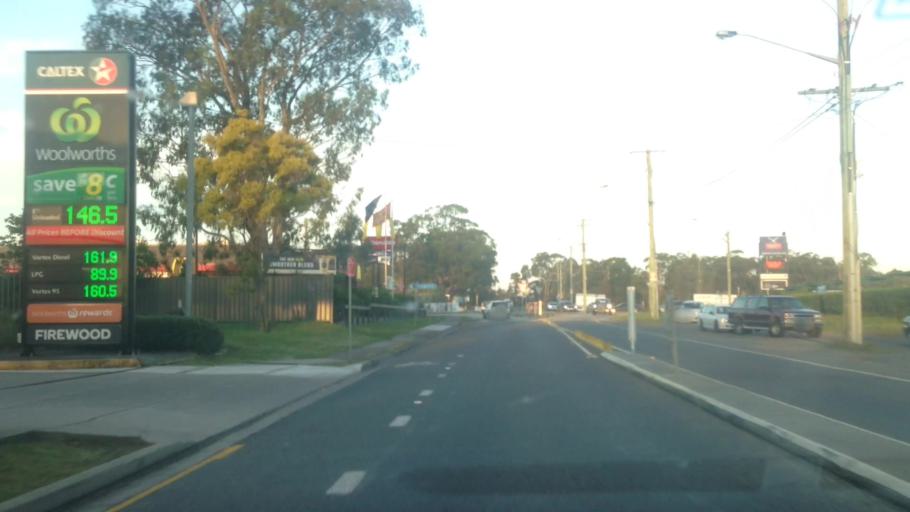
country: AU
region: New South Wales
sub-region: Lake Macquarie Shire
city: Dora Creek
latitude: -33.1118
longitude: 151.4816
